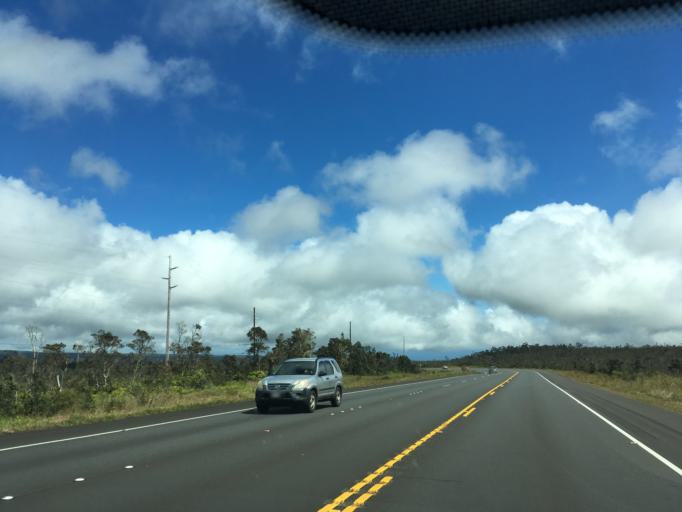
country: US
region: Hawaii
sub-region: Hawaii County
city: Wainaku
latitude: 19.6779
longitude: -155.3050
